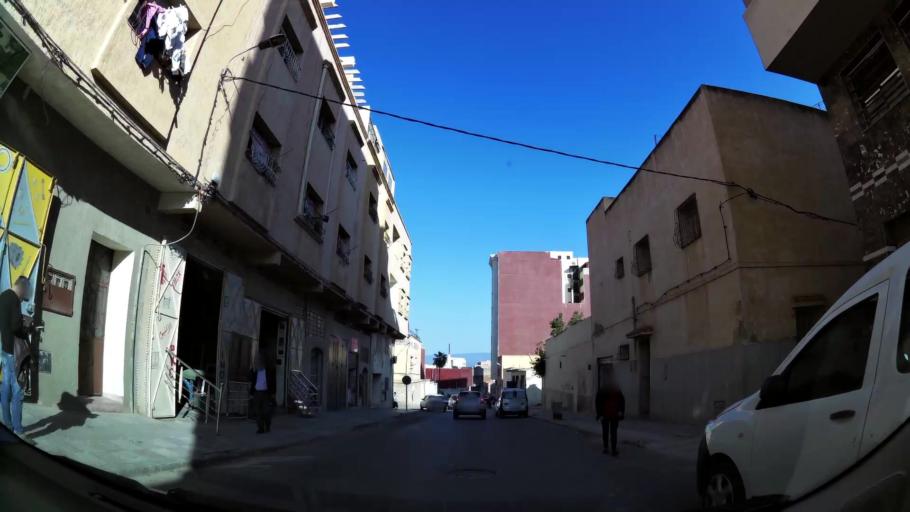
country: MA
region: Oriental
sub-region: Oujda-Angad
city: Oujda
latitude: 34.6905
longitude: -1.9103
